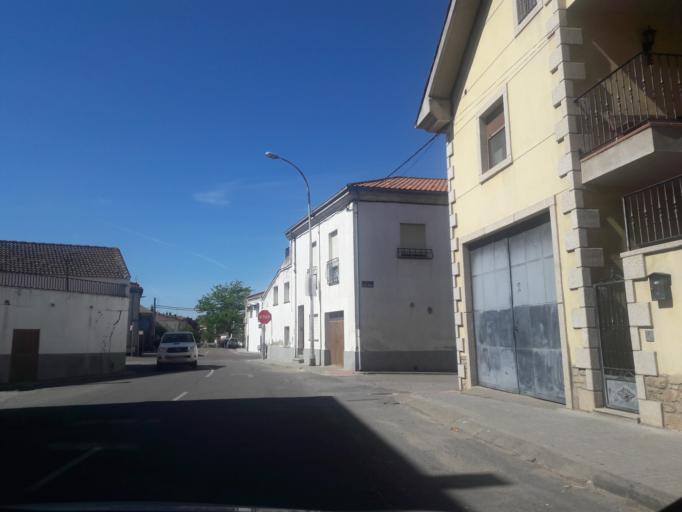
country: ES
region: Castille and Leon
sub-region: Provincia de Salamanca
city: Lumbrales
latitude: 40.9365
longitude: -6.7170
